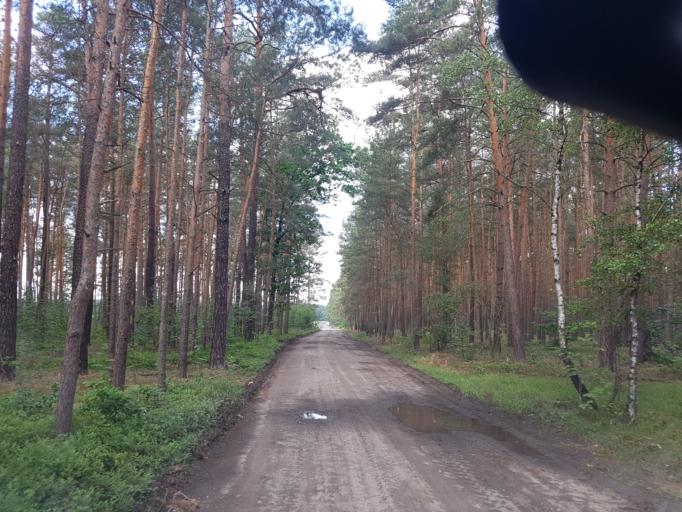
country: DE
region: Brandenburg
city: Finsterwalde
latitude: 51.5638
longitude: 13.6822
